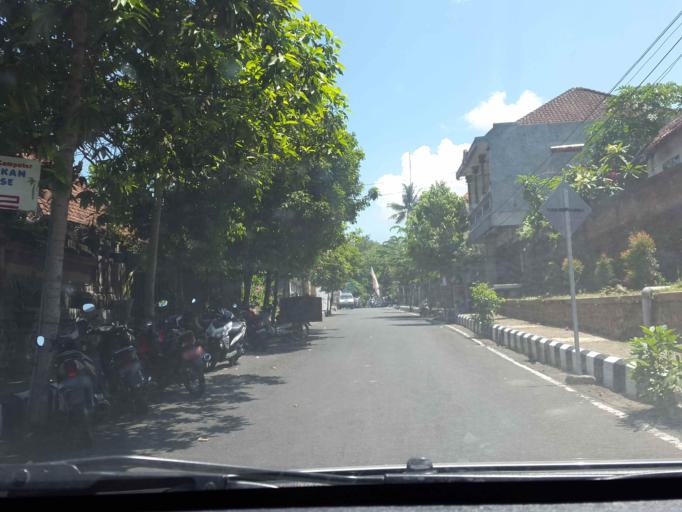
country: ID
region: Bali
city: Klungkung
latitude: -8.5384
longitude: 115.3972
